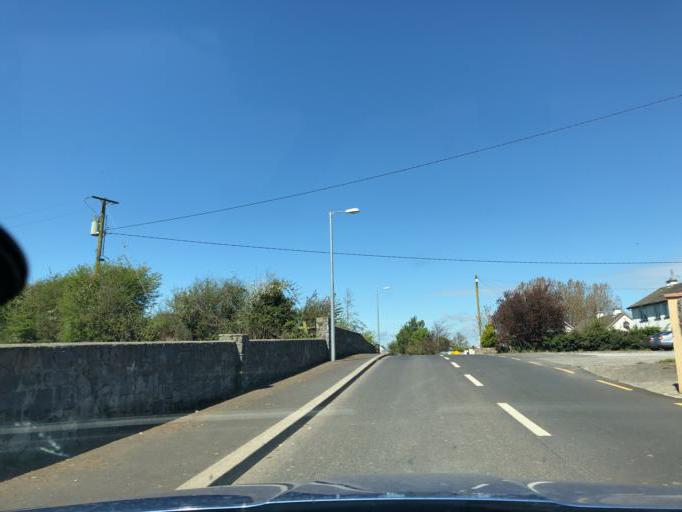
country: IE
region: Connaught
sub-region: County Galway
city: Portumna
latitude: 53.1535
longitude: -8.3801
